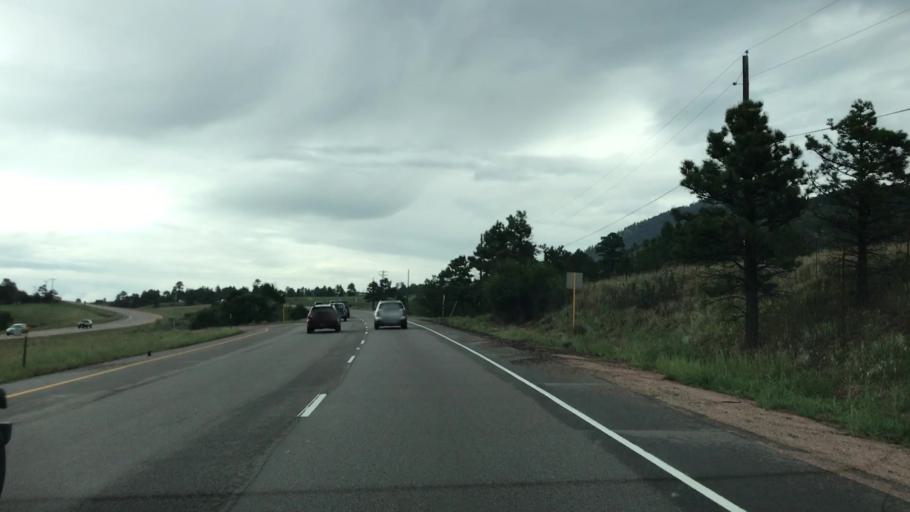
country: US
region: Colorado
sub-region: El Paso County
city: Cascade-Chipita Park
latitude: 38.9296
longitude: -104.9991
